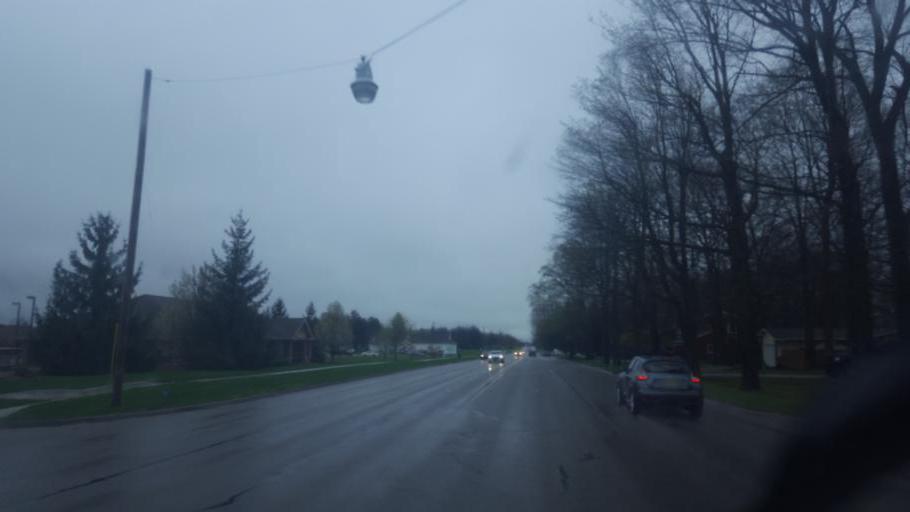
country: US
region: Michigan
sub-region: Isabella County
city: Mount Pleasant
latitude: 43.6116
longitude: -84.8022
